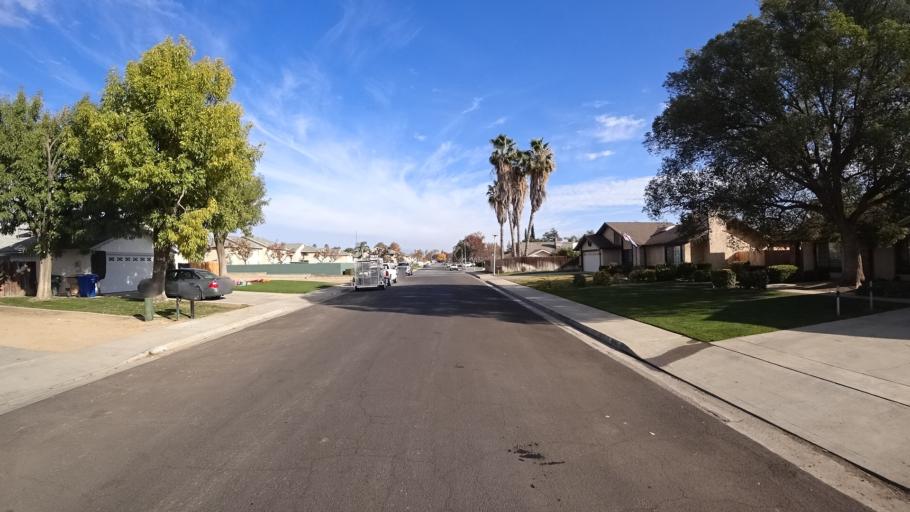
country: US
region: California
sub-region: Kern County
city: Greenacres
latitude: 35.3968
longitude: -119.1149
